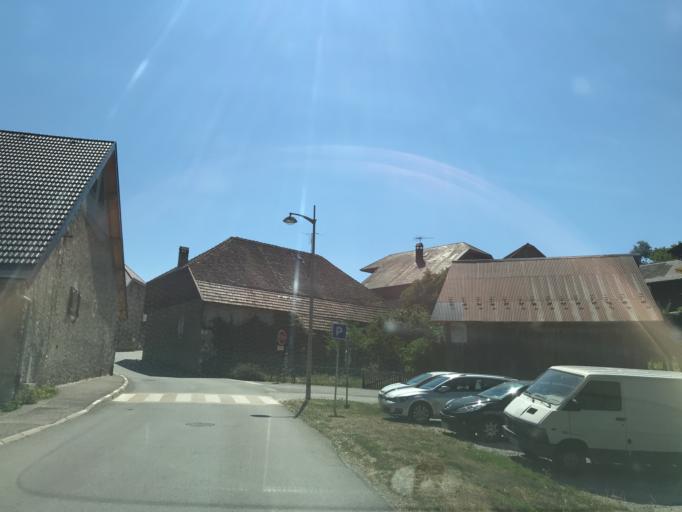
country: FR
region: Rhone-Alpes
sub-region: Departement de la Haute-Savoie
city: Villaz
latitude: 45.9352
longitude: 6.1910
